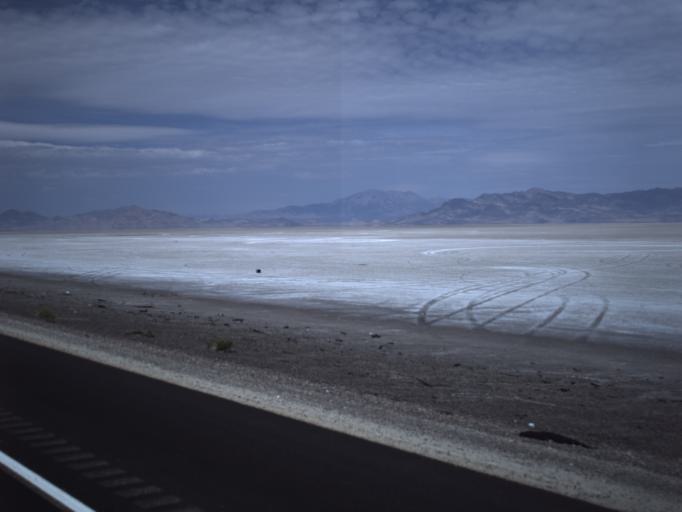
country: US
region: Utah
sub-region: Tooele County
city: Wendover
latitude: 40.7351
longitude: -113.6466
